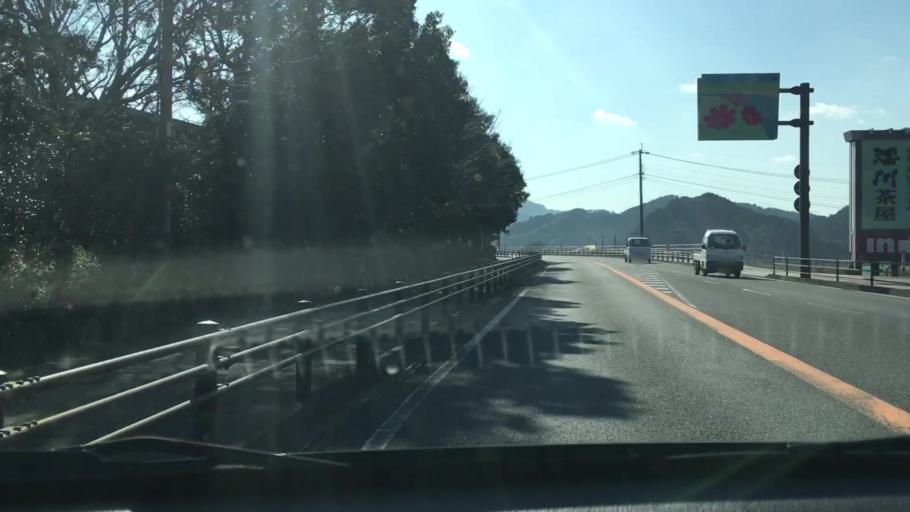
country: JP
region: Oita
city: Saiki
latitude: 32.9642
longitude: 131.8380
